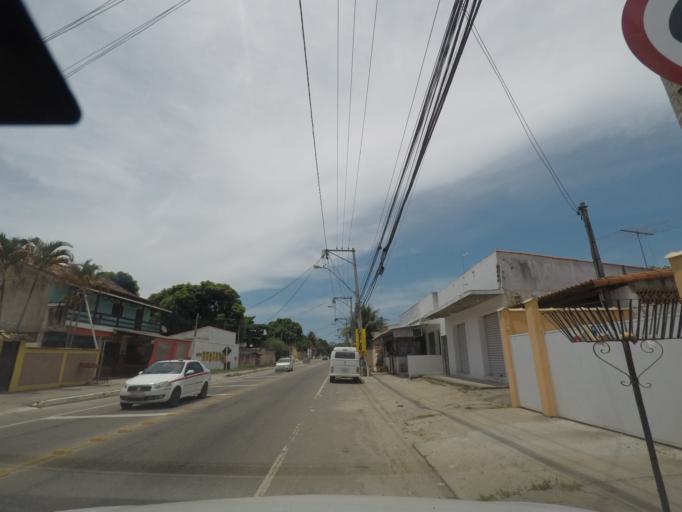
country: BR
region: Rio de Janeiro
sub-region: Marica
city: Marica
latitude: -22.9304
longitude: -42.8225
